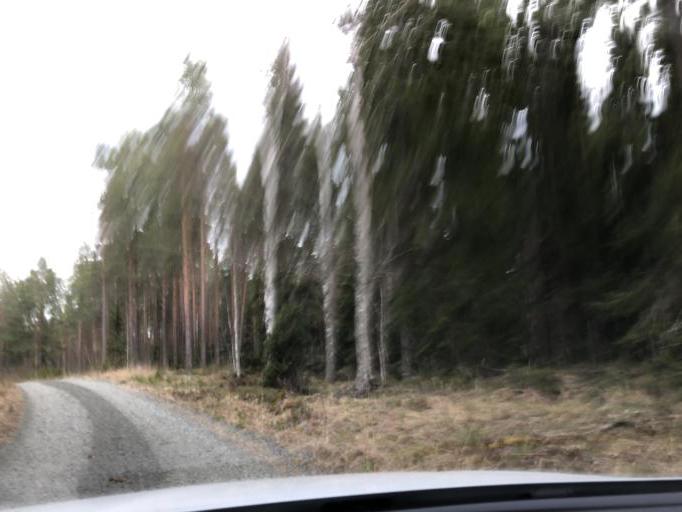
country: SE
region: Uppsala
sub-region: Heby Kommun
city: OEstervala
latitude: 60.3266
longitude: 17.1746
